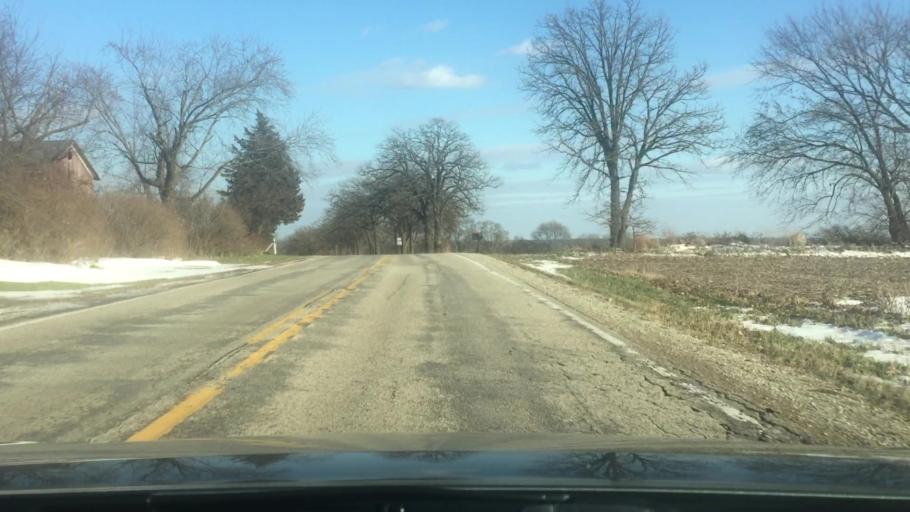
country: US
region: Wisconsin
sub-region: Jefferson County
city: Palmyra
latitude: 42.9262
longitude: -88.5474
